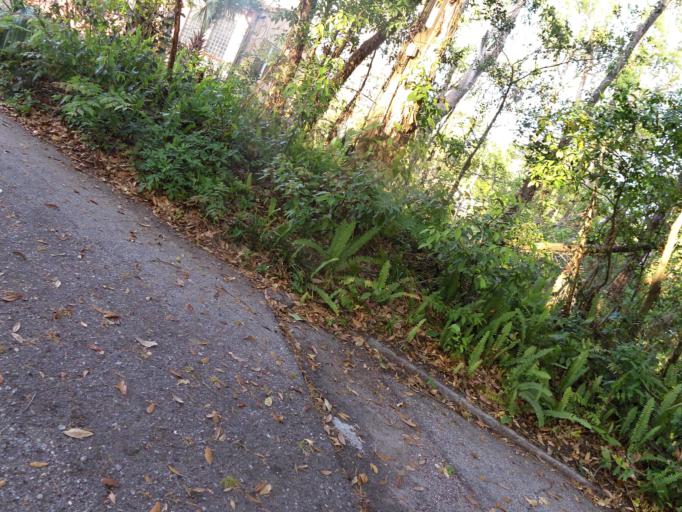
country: US
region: Florida
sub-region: Duval County
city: Jacksonville
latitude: 30.2964
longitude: -81.6486
